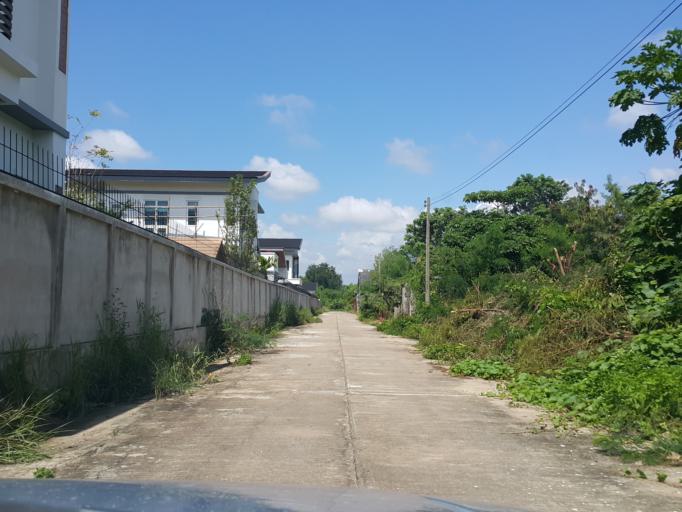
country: TH
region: Chiang Mai
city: San Kamphaeng
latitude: 18.7256
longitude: 99.0982
